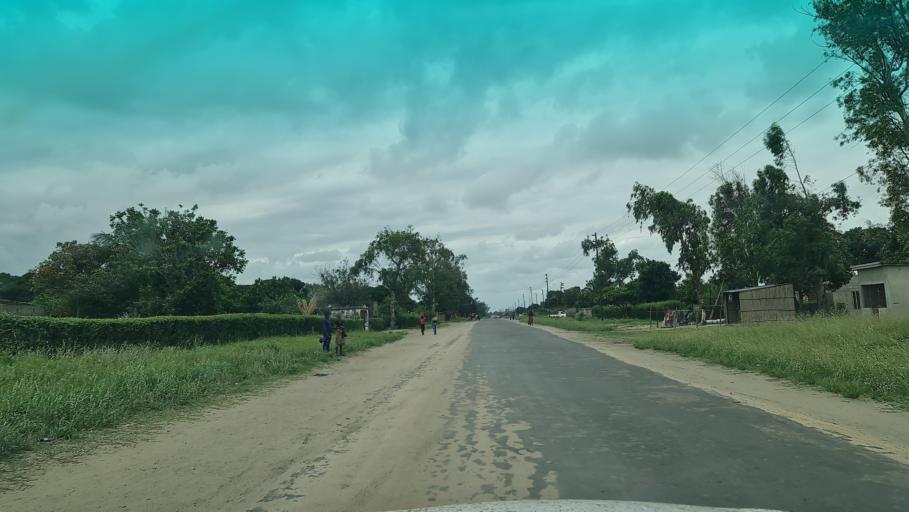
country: MZ
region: Maputo
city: Manhica
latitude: -25.4438
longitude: 32.7737
